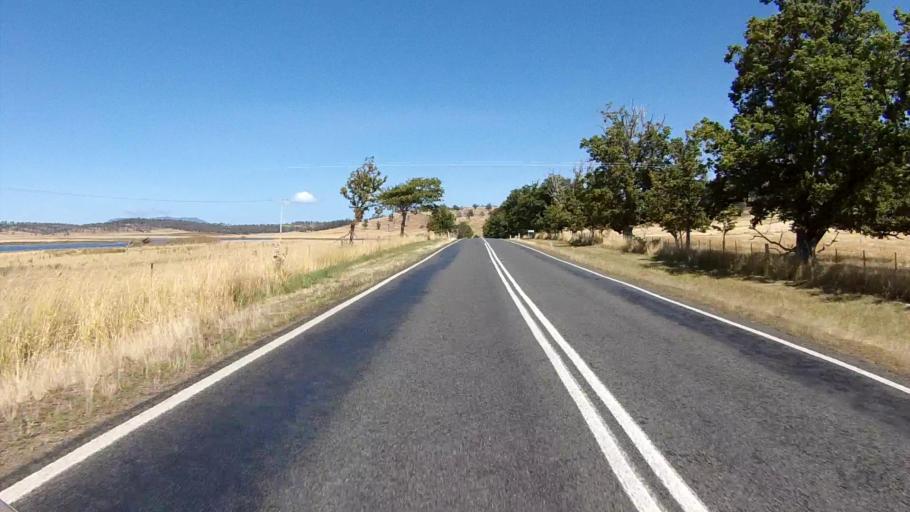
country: AU
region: Tasmania
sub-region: Sorell
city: Sorell
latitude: -42.4827
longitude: 147.9334
